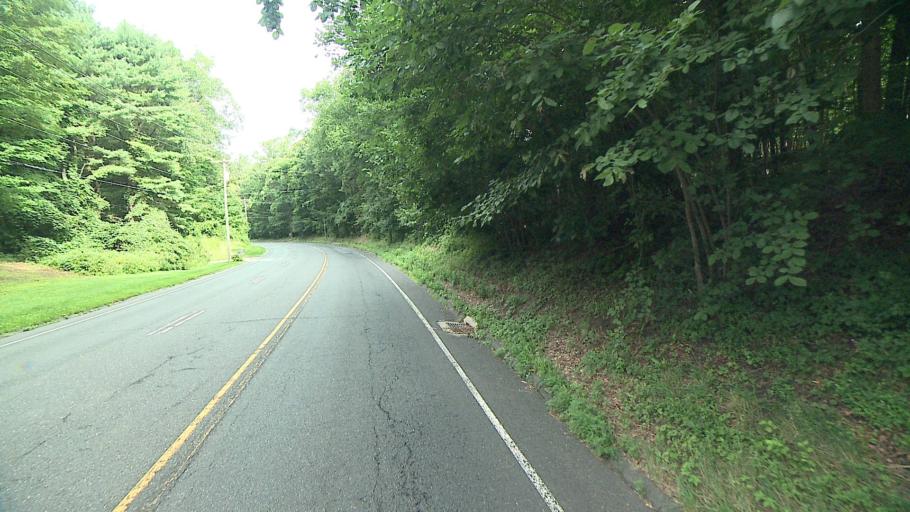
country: US
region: Connecticut
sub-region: Litchfield County
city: Woodbury Center
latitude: 41.5323
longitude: -73.1887
